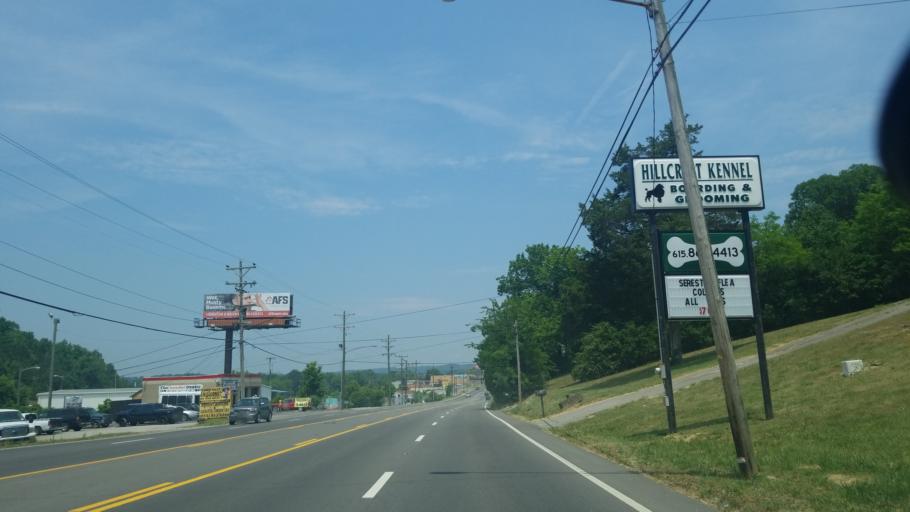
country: US
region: Tennessee
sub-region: Davidson County
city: Goodlettsville
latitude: 36.2536
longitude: -86.7577
